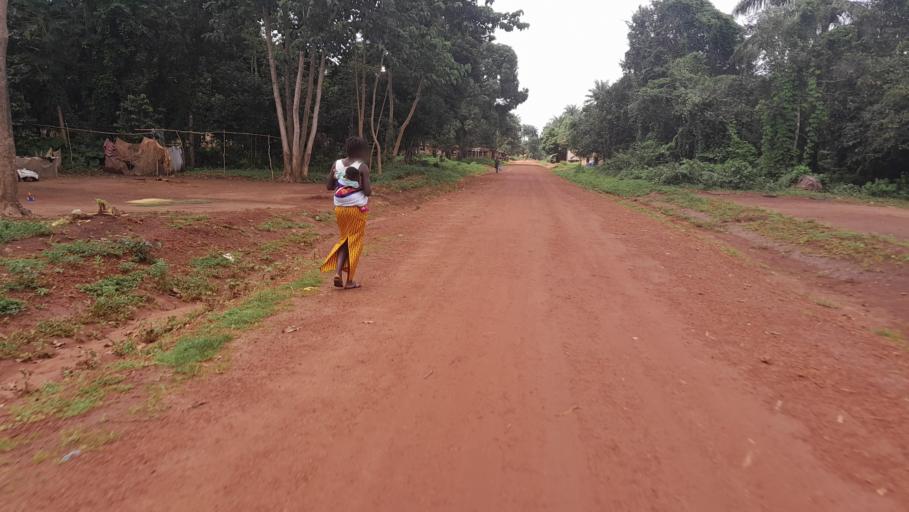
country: GN
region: Boke
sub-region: Boffa
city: Boffa
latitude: 10.0095
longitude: -13.8869
